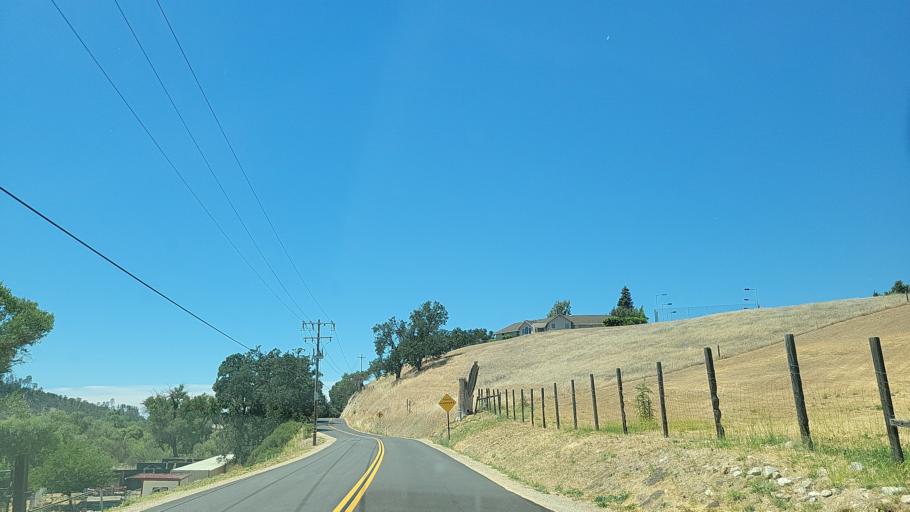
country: US
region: California
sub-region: San Luis Obispo County
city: Atascadero
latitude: 35.4889
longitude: -120.6383
